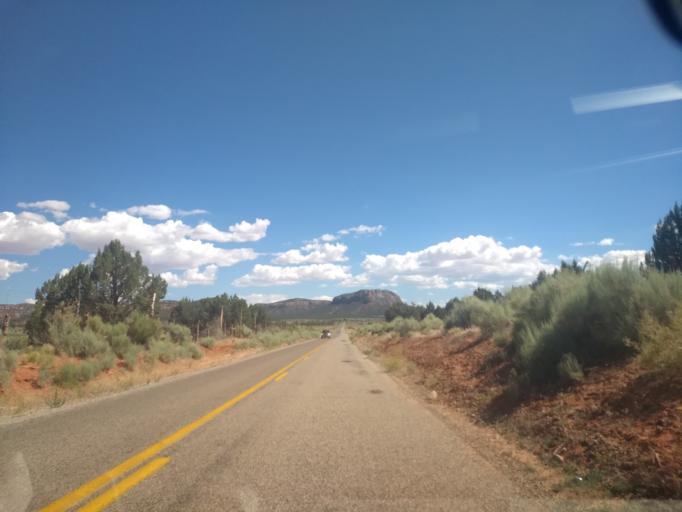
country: US
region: Utah
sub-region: Washington County
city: Hildale
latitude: 36.9608
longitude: -112.8746
